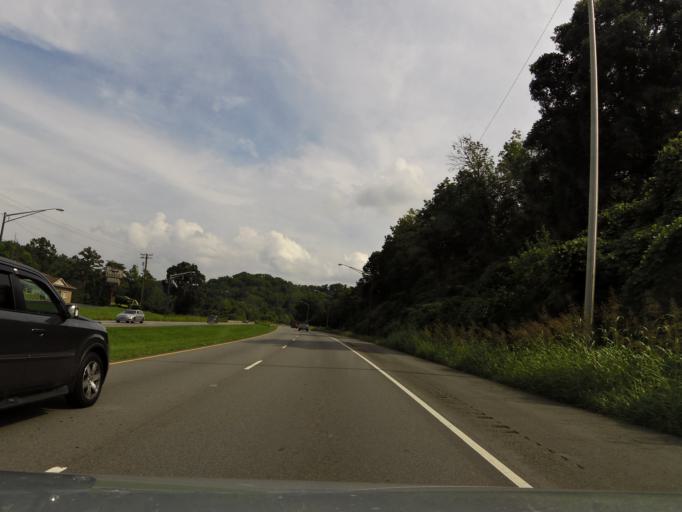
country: US
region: Tennessee
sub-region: Knox County
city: Knoxville
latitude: 35.8976
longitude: -83.9538
